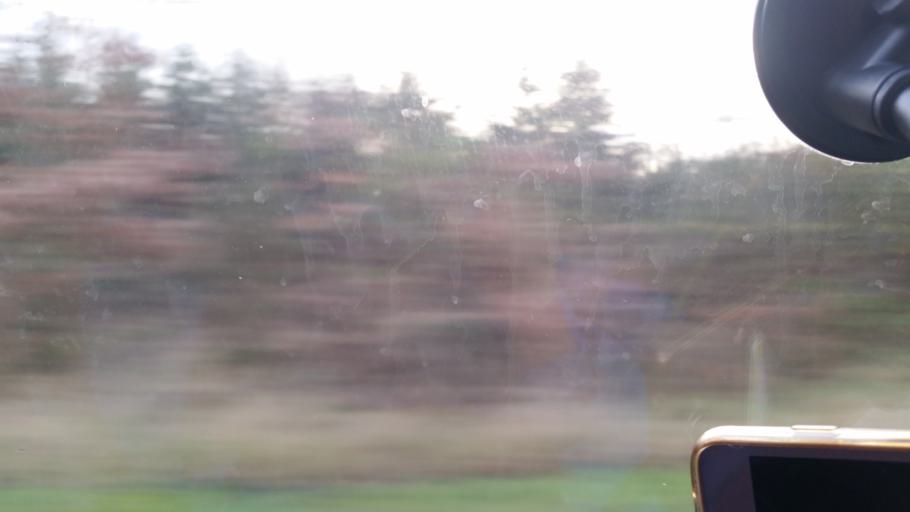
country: IE
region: Ulster
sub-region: County Monaghan
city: Carrickmacross
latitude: 53.9611
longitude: -6.6848
